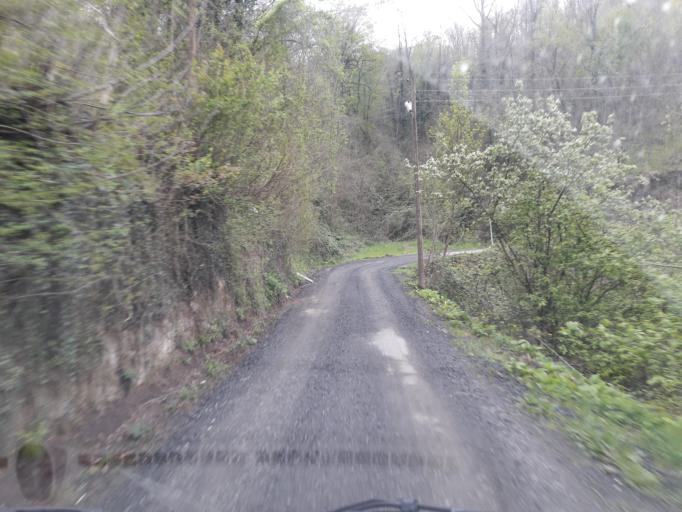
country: TR
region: Trabzon
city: Duzkoy
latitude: 40.9266
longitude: 39.4823
